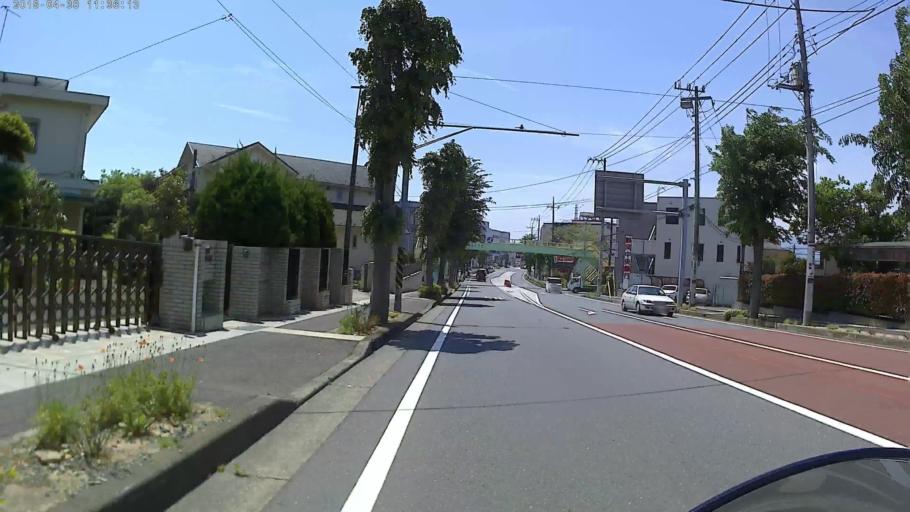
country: JP
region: Kanagawa
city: Zama
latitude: 35.4840
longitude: 139.3959
